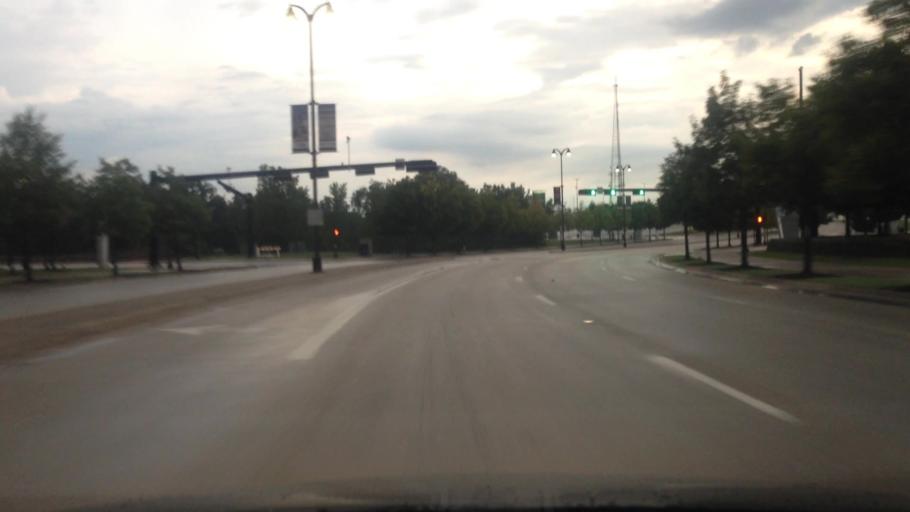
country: US
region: Texas
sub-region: Tarrant County
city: Arlington
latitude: 32.7470
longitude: -97.0896
